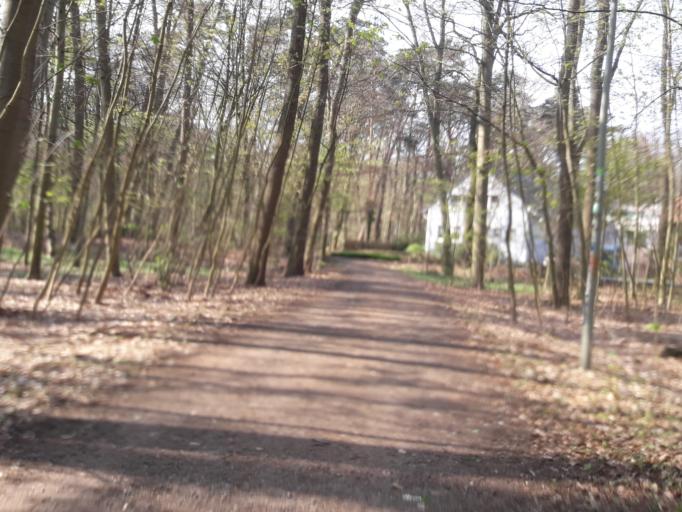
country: DE
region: North Rhine-Westphalia
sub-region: Regierungsbezirk Detmold
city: Paderborn
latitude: 51.7324
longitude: 8.7424
